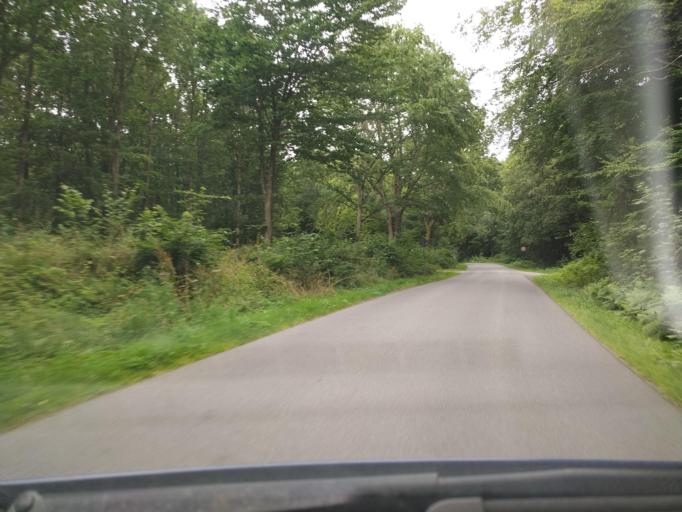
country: DE
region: Schleswig-Holstein
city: Neuberend
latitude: 54.5196
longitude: 9.5234
